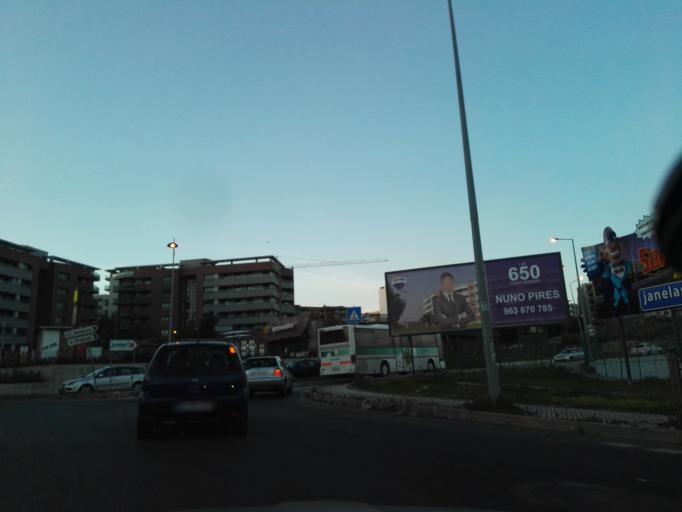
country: PT
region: Lisbon
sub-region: Vila Franca de Xira
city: Vialonga
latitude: 38.8872
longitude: -9.0457
